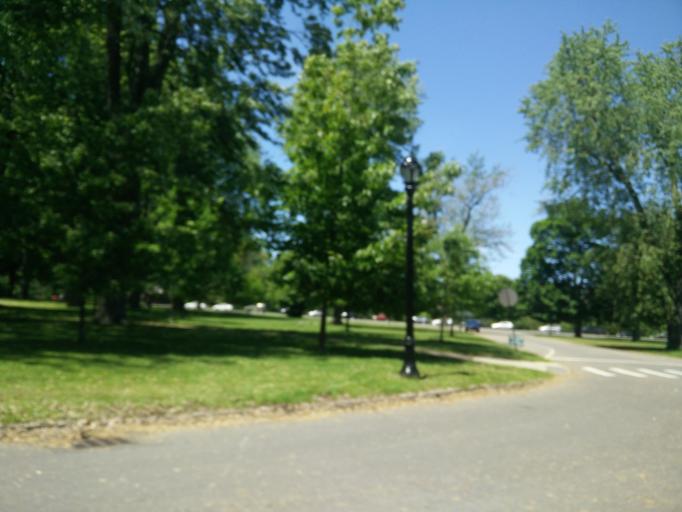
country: US
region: New York
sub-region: Erie County
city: West Seneca
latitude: 42.8489
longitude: -78.8047
